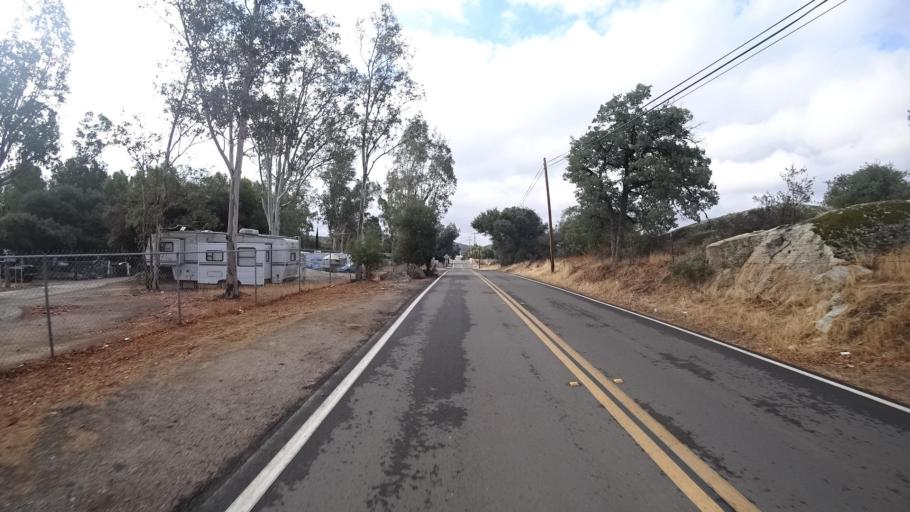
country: MX
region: Baja California
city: Tecate
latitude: 32.6246
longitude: -116.6135
